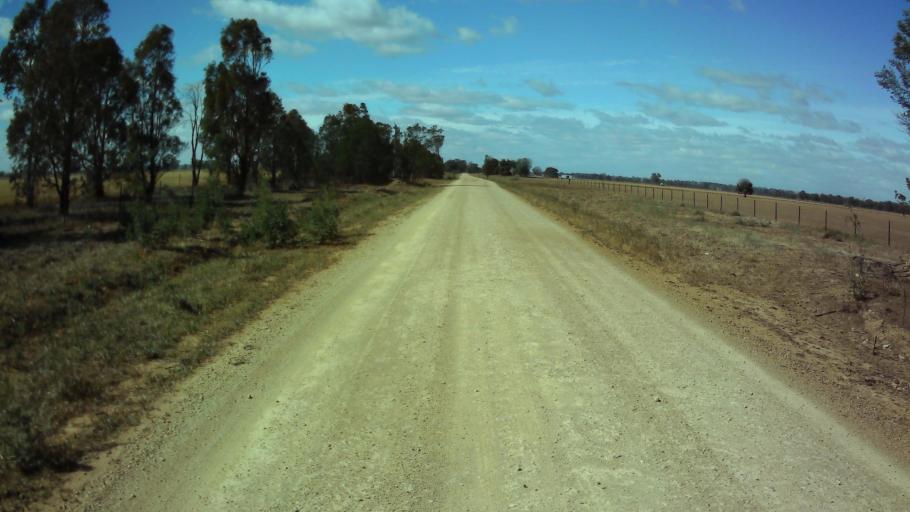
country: AU
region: New South Wales
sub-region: Weddin
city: Grenfell
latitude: -34.0168
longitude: 148.3198
